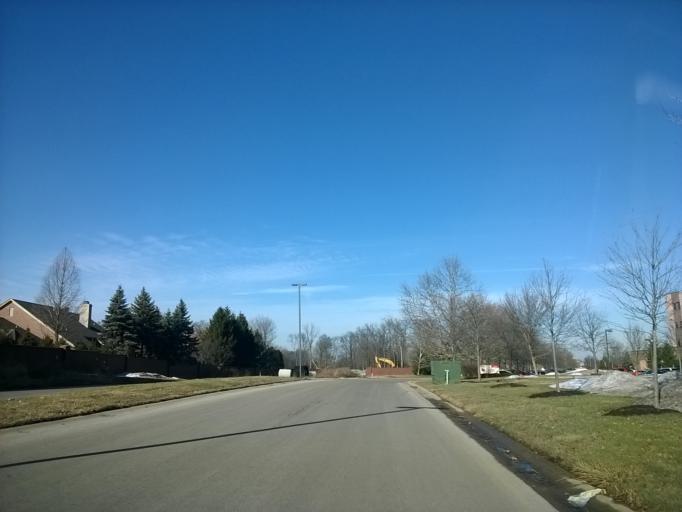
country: US
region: Indiana
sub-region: Marion County
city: Meridian Hills
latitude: 39.9381
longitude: -86.1605
